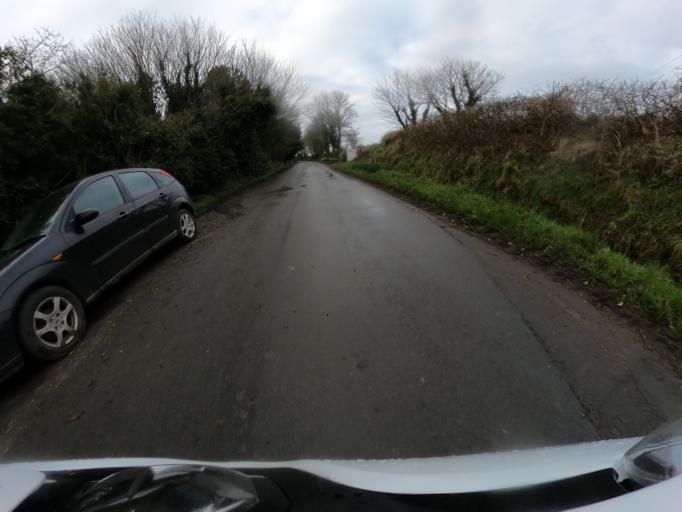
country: IM
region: Ramsey
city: Ramsey
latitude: 54.3632
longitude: -4.4937
